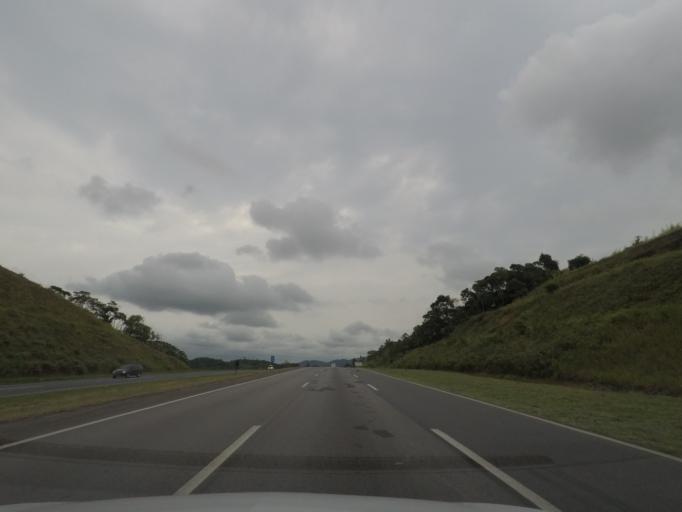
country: BR
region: Sao Paulo
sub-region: Juquia
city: Juquia
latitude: -24.3315
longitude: -47.6098
